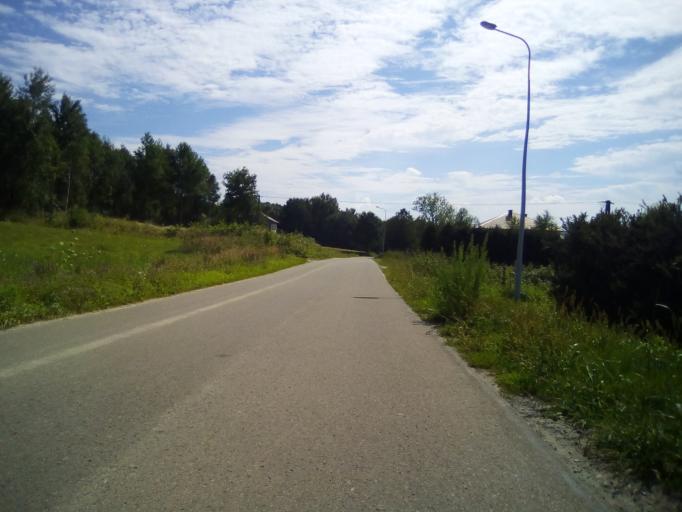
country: PL
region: Subcarpathian Voivodeship
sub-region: Powiat strzyzowski
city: Konieczkowa
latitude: 49.8218
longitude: 21.9266
